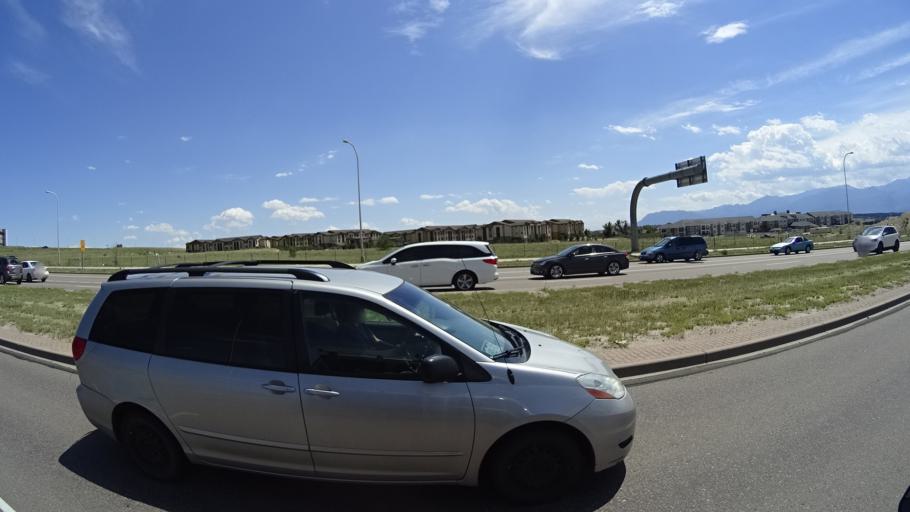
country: US
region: Colorado
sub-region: El Paso County
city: Black Forest
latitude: 38.9404
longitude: -104.7234
